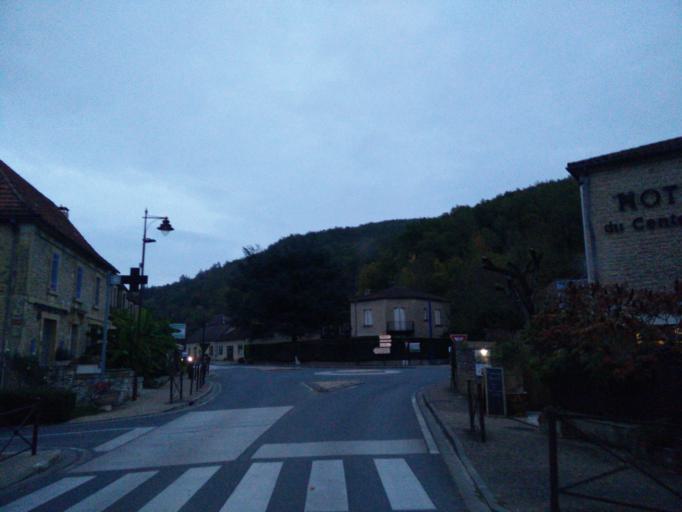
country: FR
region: Aquitaine
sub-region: Departement de la Dordogne
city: Saint-Cyprien
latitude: 44.9347
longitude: 1.0154
